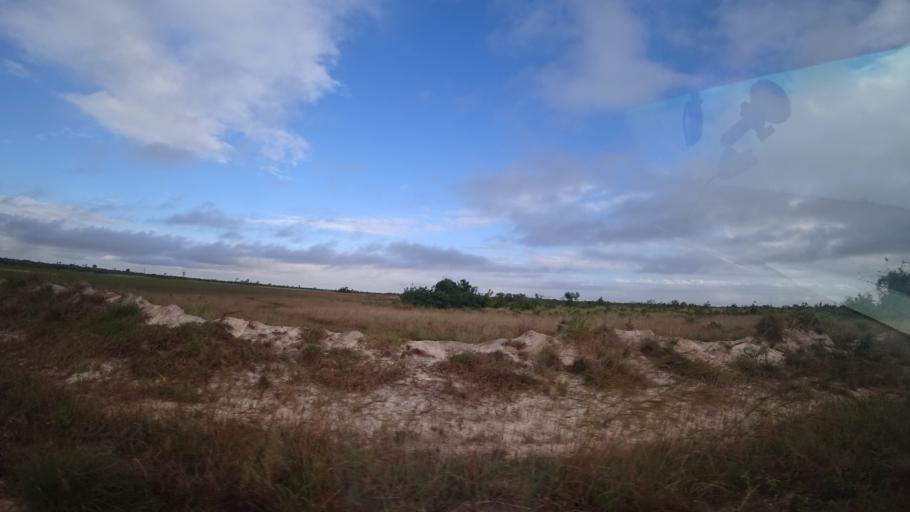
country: MZ
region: Sofala
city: Beira
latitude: -19.6262
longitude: 35.0603
